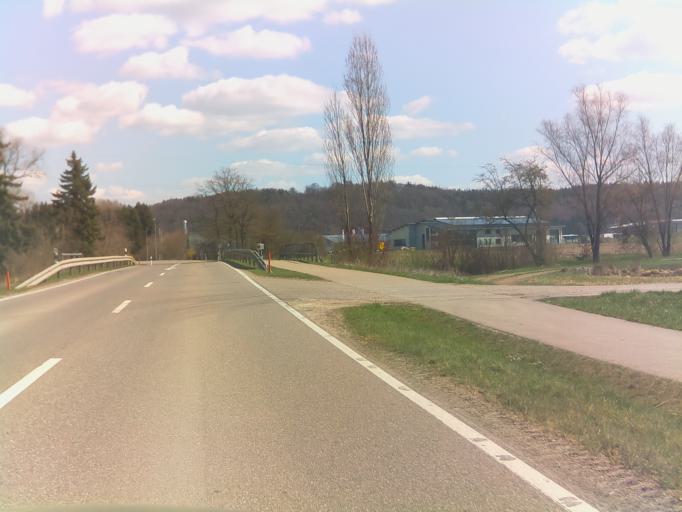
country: DE
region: Bavaria
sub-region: Swabia
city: Todtenweis
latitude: 48.5120
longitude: 10.9033
